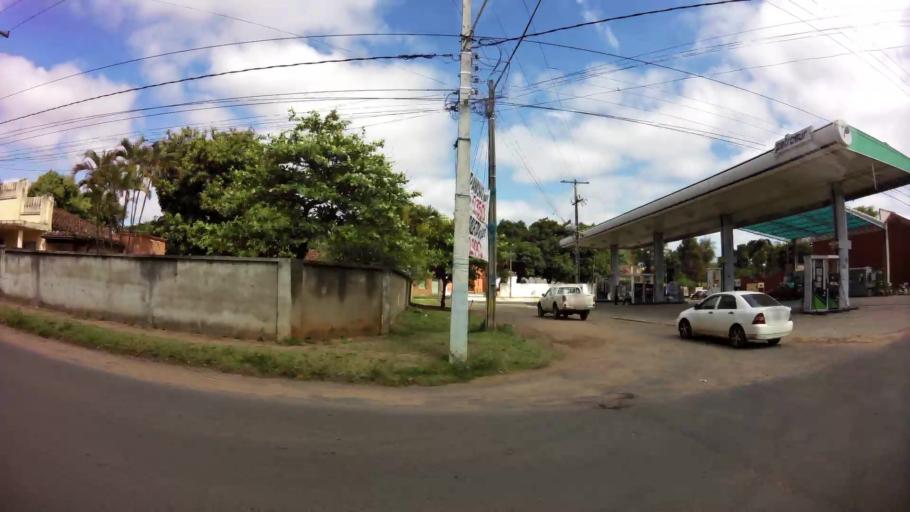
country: PY
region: Central
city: San Lorenzo
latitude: -25.2722
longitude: -57.4956
